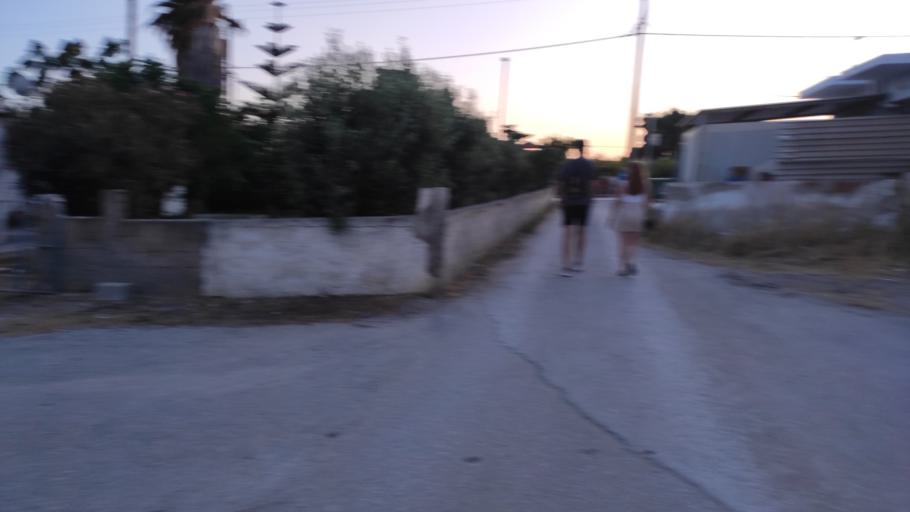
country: GR
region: South Aegean
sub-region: Nomos Dodekanisou
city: Kos
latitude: 36.9108
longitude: 27.2795
